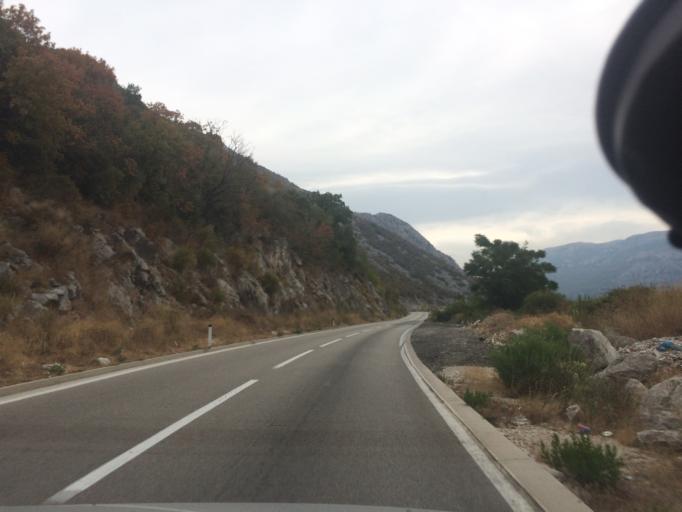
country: ME
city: Lipci
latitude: 42.4963
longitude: 18.6496
